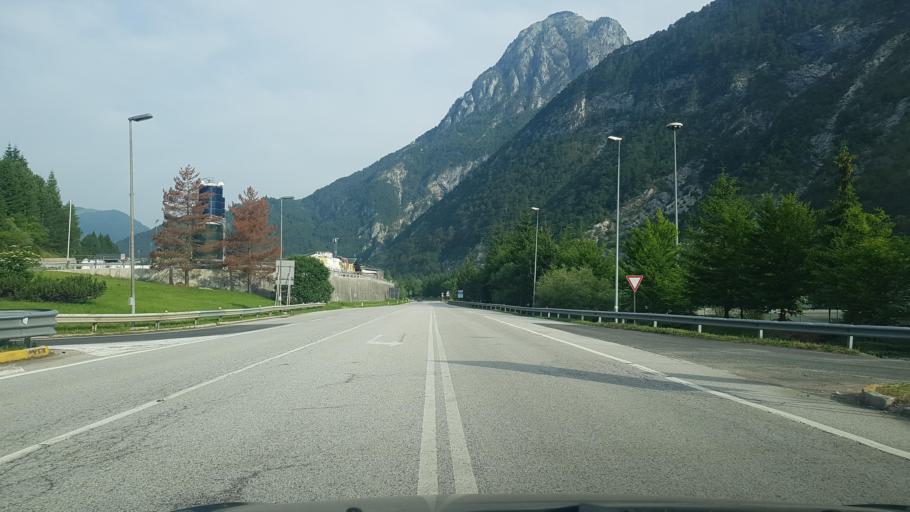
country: IT
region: Friuli Venezia Giulia
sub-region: Provincia di Udine
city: Pontebba
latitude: 46.5092
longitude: 13.3407
